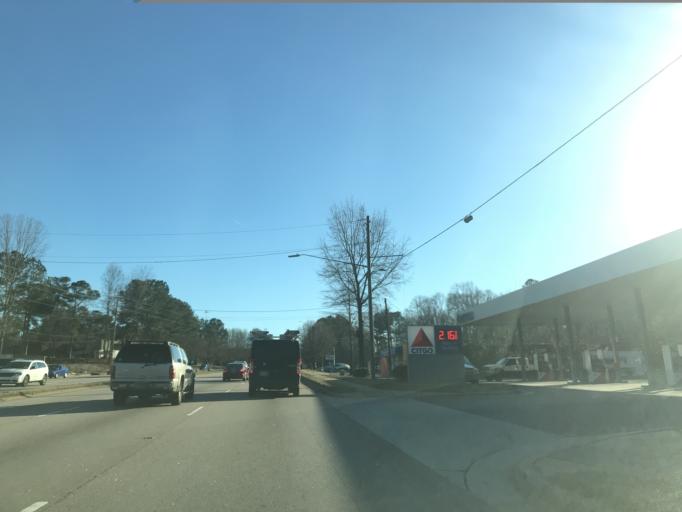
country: US
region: North Carolina
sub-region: Wake County
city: Raleigh
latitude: 35.7448
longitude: -78.6490
